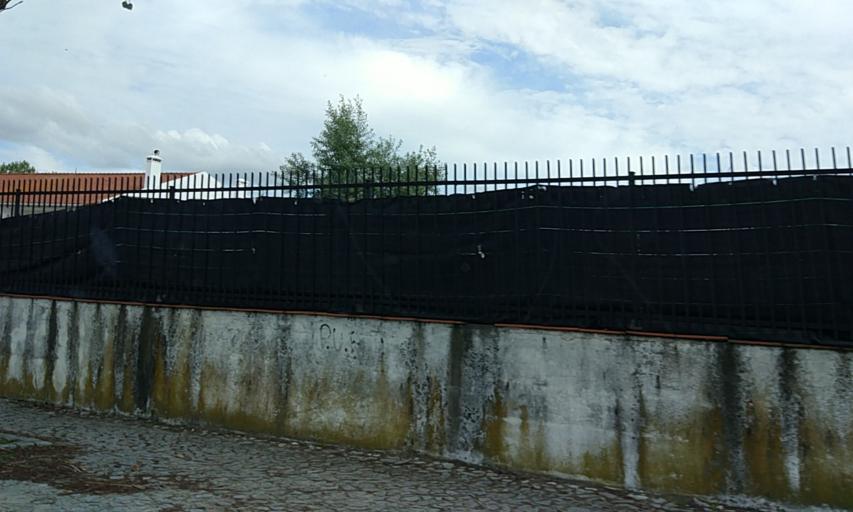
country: PT
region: Evora
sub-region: Evora
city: Evora
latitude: 38.5674
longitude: -7.9285
